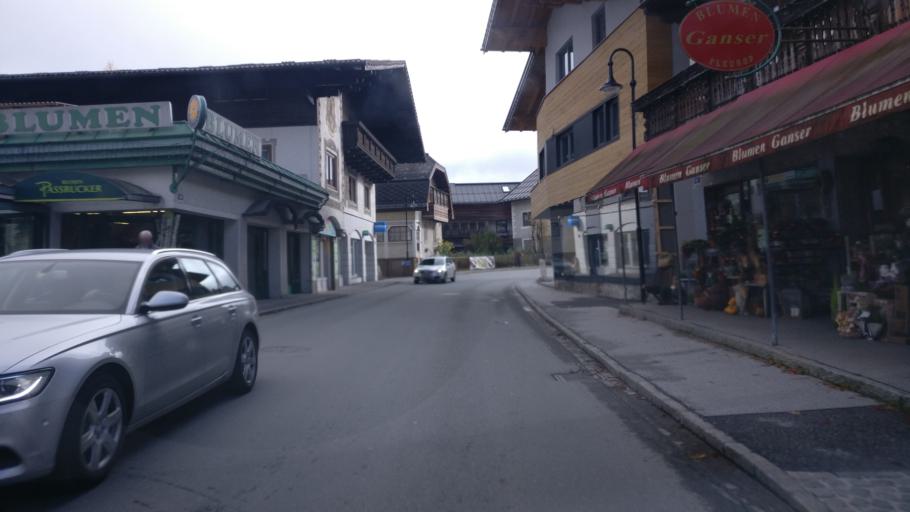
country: AT
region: Salzburg
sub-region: Politischer Bezirk Sankt Johann im Pongau
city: Altenmarkt im Pongau
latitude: 47.3791
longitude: 13.4214
